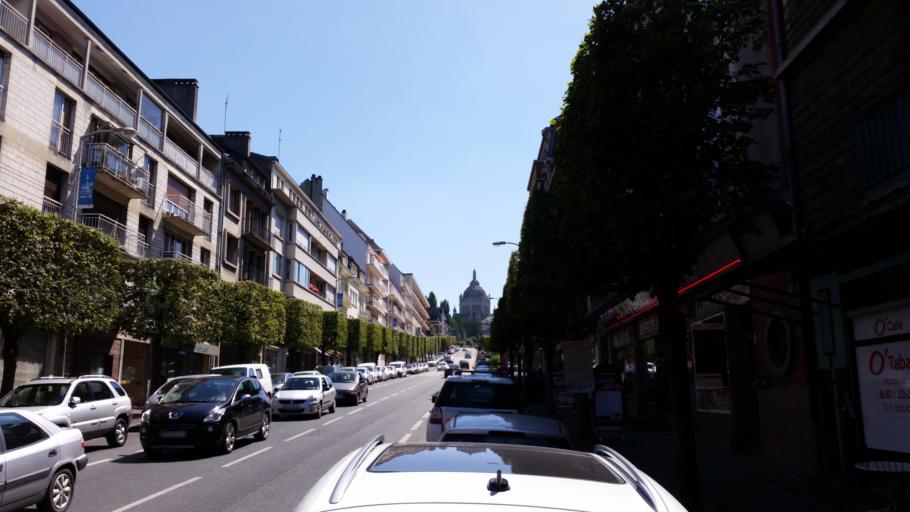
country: FR
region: Lower Normandy
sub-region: Departement du Calvados
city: Lisieux
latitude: 49.1435
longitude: 0.2294
